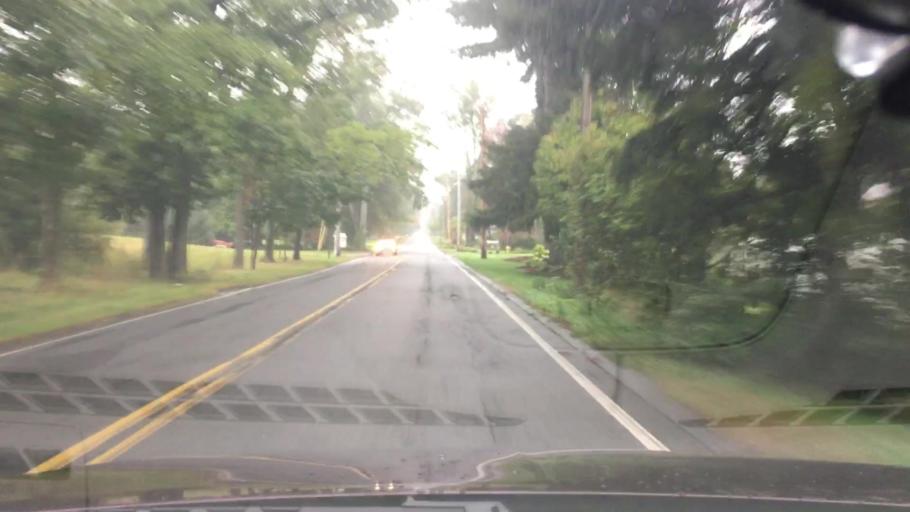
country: US
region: Massachusetts
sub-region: Hampden County
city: East Longmeadow
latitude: 42.0380
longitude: -72.4961
